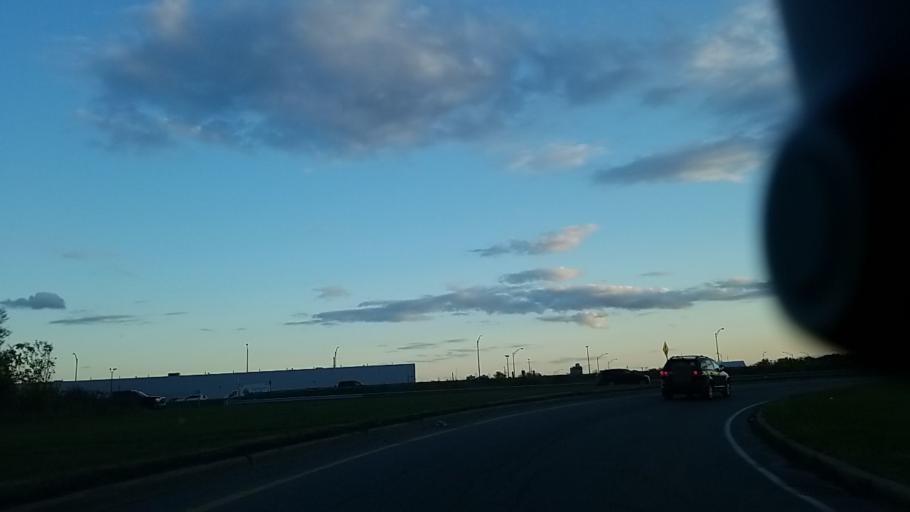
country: CA
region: Quebec
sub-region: Laval
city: Laval
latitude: 45.5868
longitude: -73.7357
